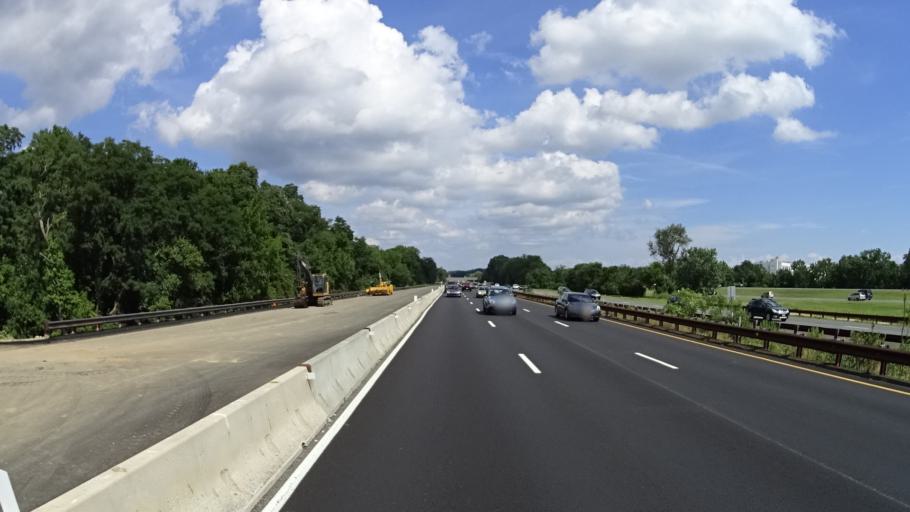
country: US
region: New Jersey
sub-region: Monmouth County
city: Tinton Falls
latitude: 40.2914
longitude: -74.0916
